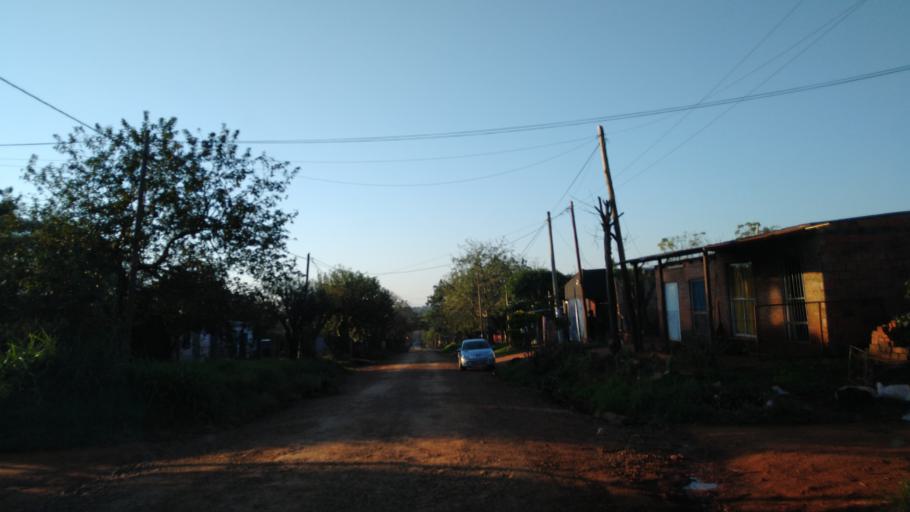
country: AR
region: Misiones
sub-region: Departamento de Capital
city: Posadas
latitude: -27.4246
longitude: -55.9209
